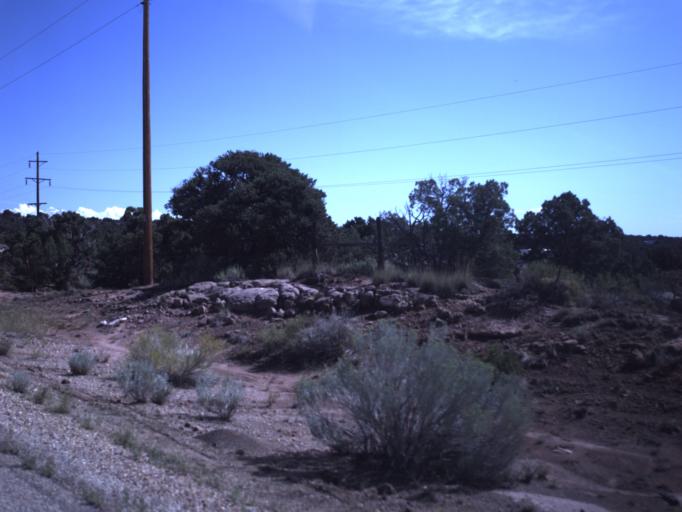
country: US
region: Utah
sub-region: Duchesne County
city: Duchesne
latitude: 40.2967
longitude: -110.3742
